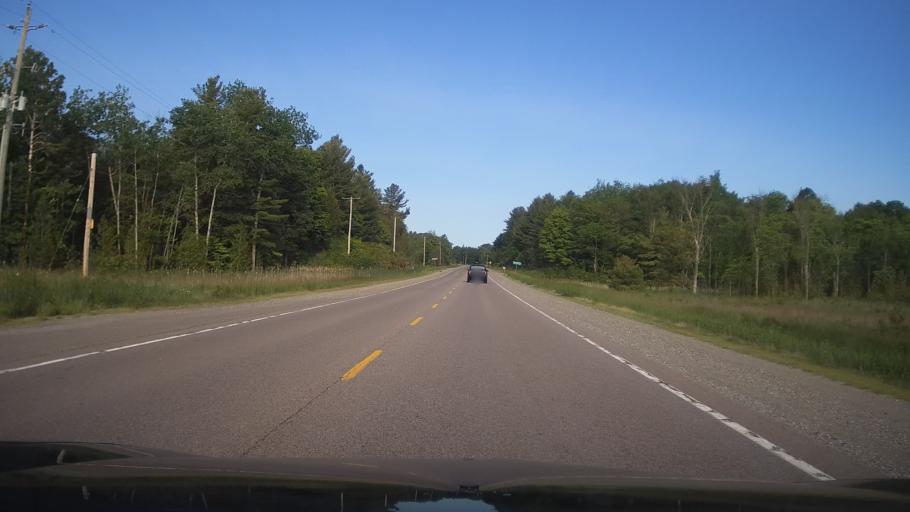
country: CA
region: Ontario
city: Skatepark
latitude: 44.7542
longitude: -76.9006
